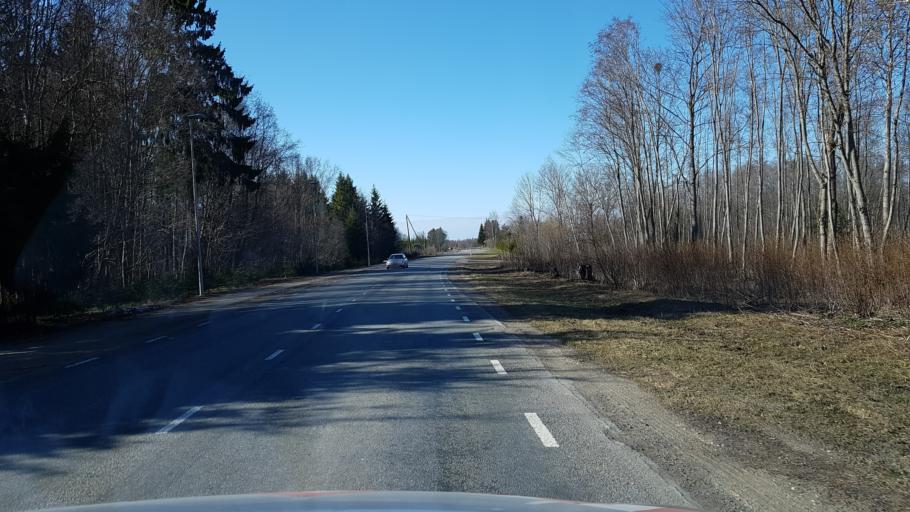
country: EE
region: Laeaene-Virumaa
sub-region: Haljala vald
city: Haljala
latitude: 59.4438
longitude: 26.2540
